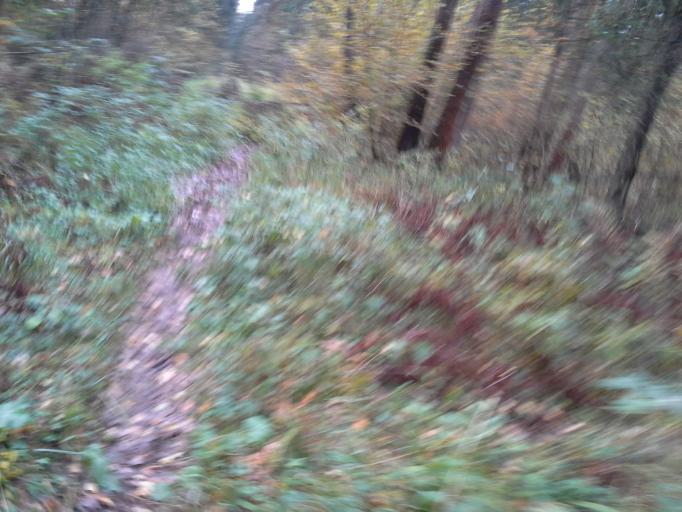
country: RU
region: Moskovskaya
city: Nazar'yevo
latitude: 55.6665
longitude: 37.0190
